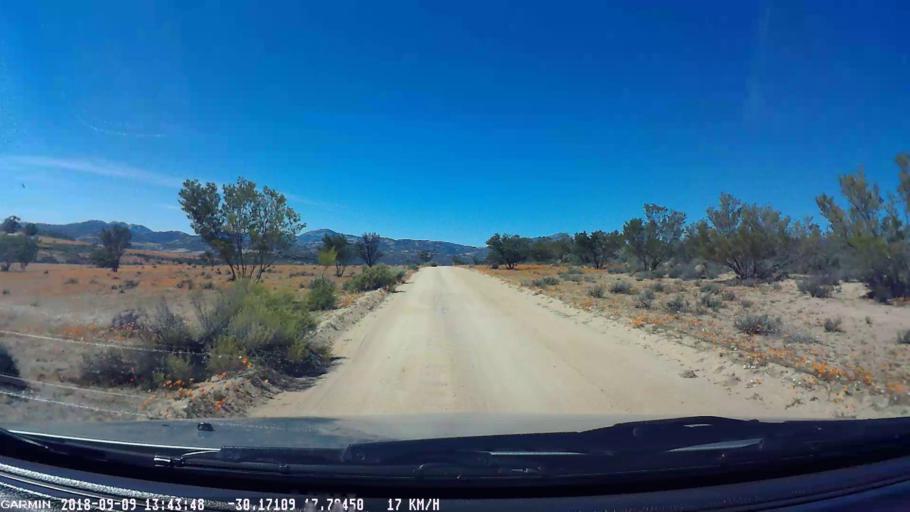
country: ZA
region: Northern Cape
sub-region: Namakwa District Municipality
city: Garies
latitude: -30.1708
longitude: 17.7958
